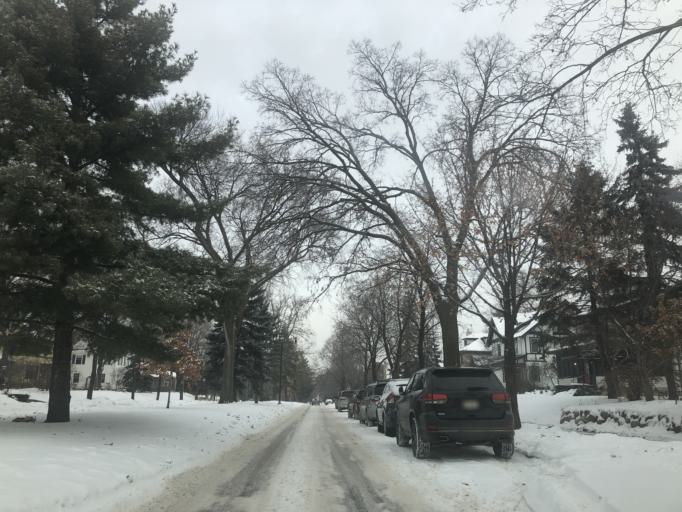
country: US
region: Minnesota
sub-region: Hennepin County
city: Richfield
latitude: 44.9251
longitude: -93.2934
